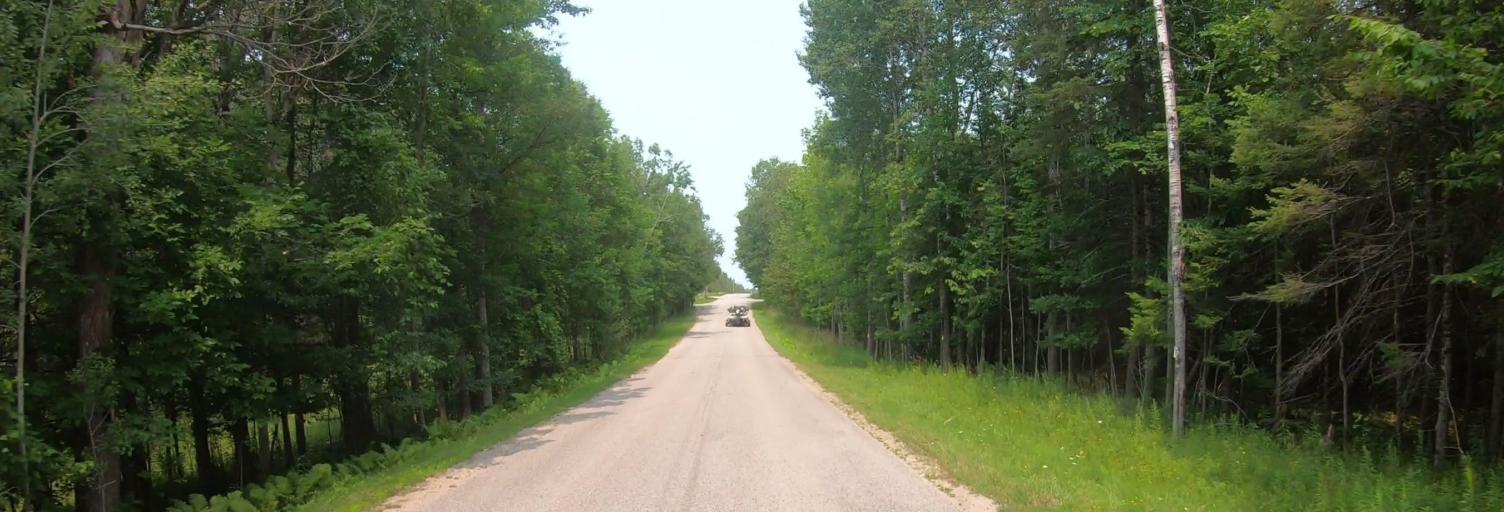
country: CA
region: Ontario
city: Thessalon
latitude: 46.0407
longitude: -83.6664
